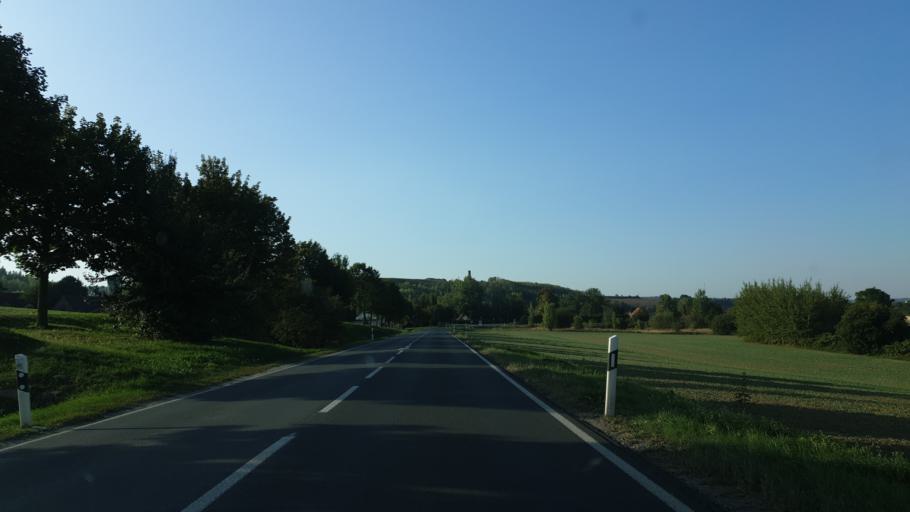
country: DE
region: Thuringia
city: Caaschwitz
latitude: 50.9421
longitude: 11.9928
